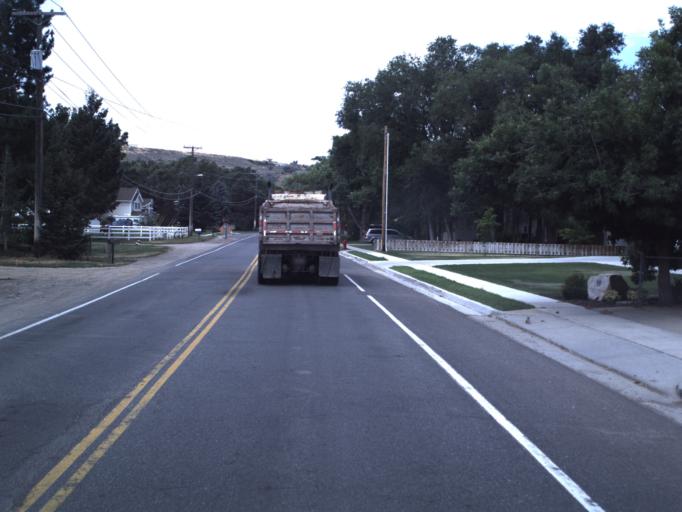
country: US
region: Utah
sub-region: Davis County
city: South Weber
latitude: 41.1346
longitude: -111.9512
